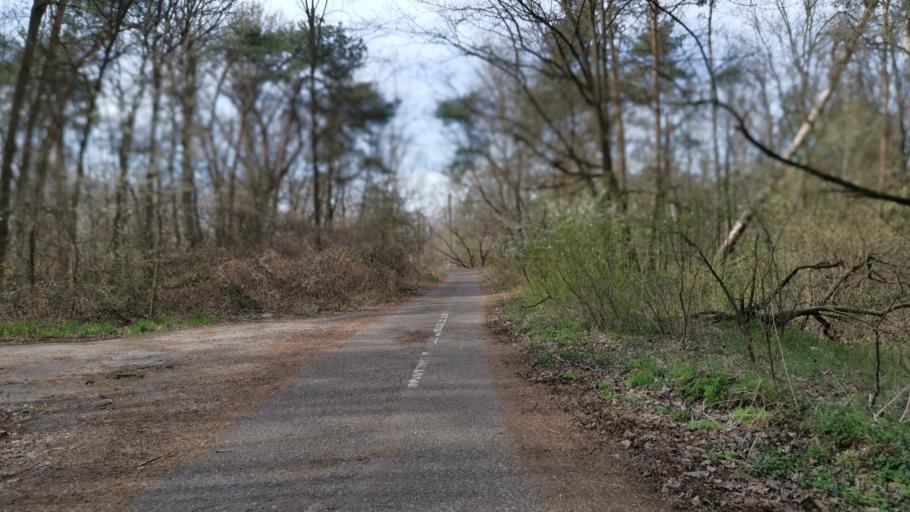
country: SK
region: Trnavsky
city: Gbely
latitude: 48.6677
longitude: 17.0532
